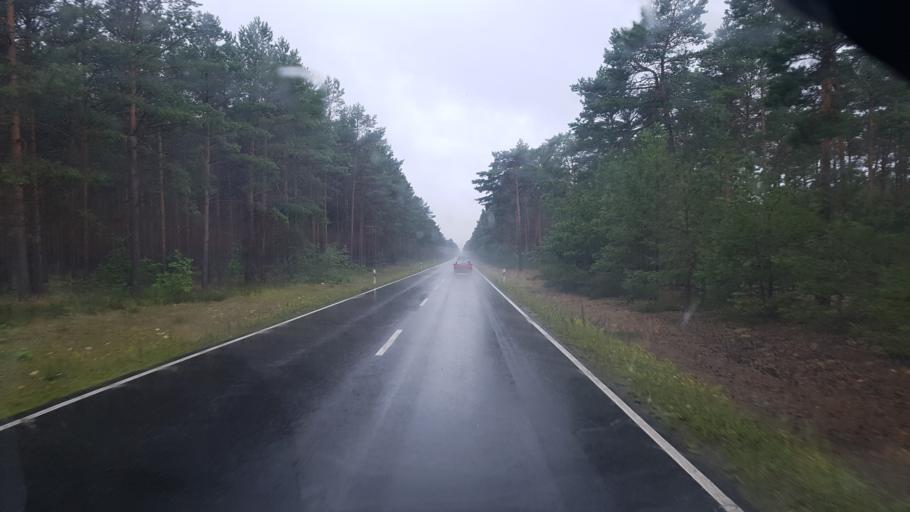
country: DE
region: Brandenburg
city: Teupitz
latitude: 52.0582
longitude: 13.6350
